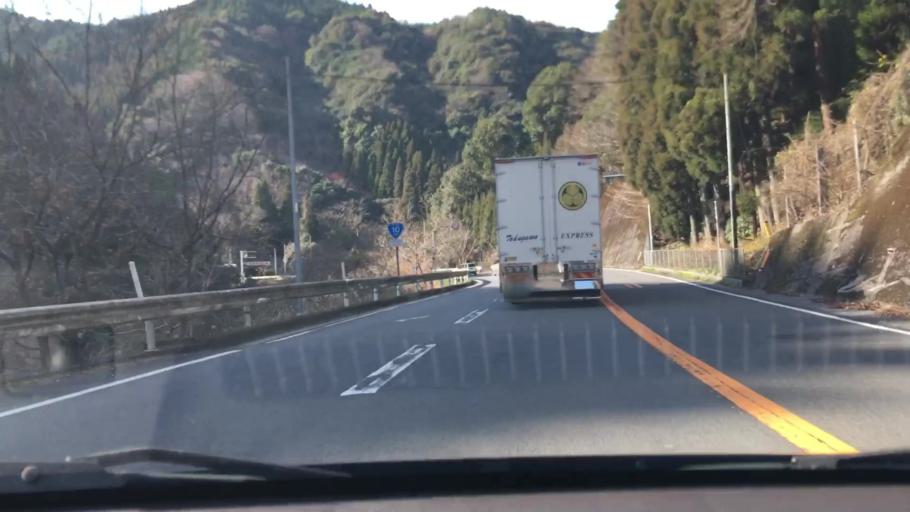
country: JP
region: Oita
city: Tsukumiura
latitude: 32.9988
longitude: 131.7832
